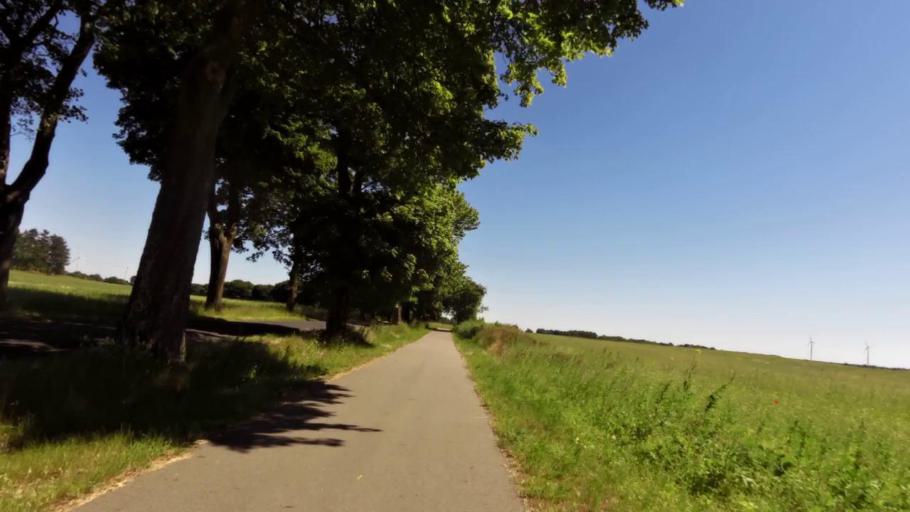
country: PL
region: West Pomeranian Voivodeship
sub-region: Powiat kolobrzeski
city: Goscino
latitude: 54.0355
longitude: 15.6752
